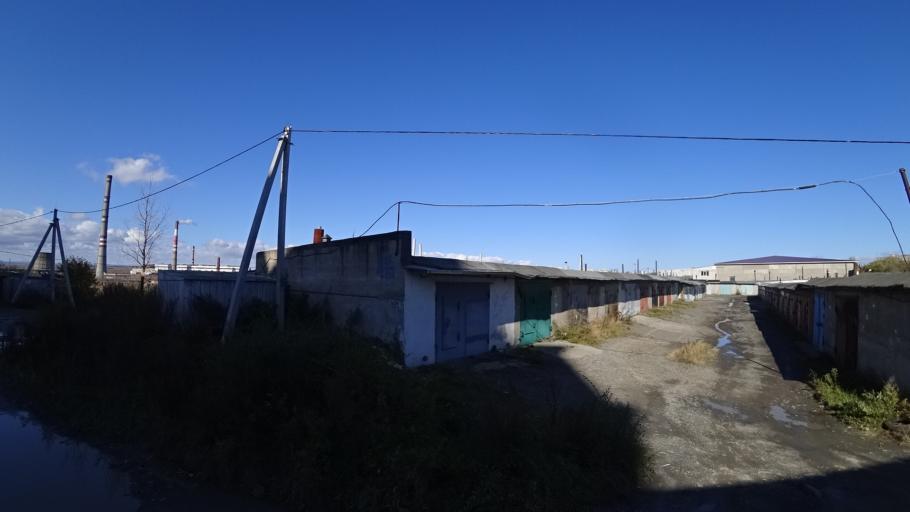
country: RU
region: Khabarovsk Krai
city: Amursk
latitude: 50.2193
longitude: 136.8951
